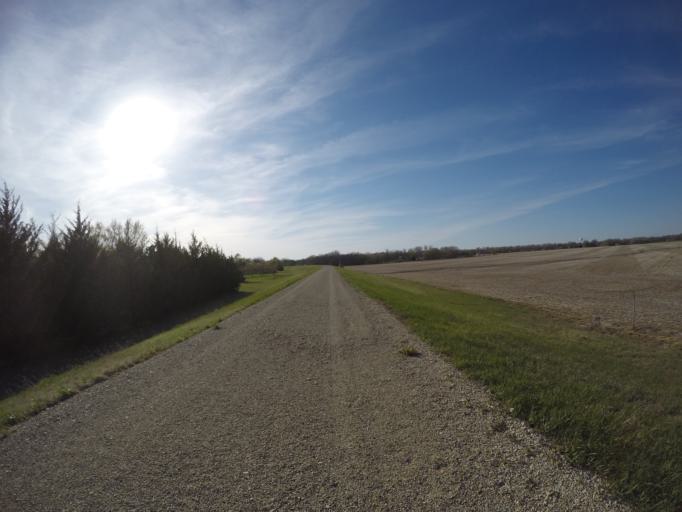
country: US
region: Kansas
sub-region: Saline County
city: Salina
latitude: 38.8641
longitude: -97.6017
